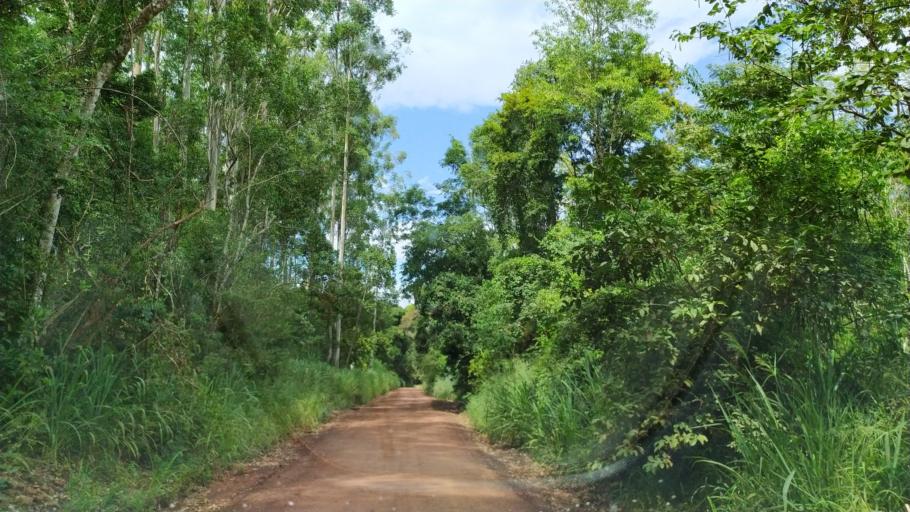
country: AR
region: Misiones
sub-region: Departamento de Eldorado
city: Eldorado
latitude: -26.4556
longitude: -54.5954
